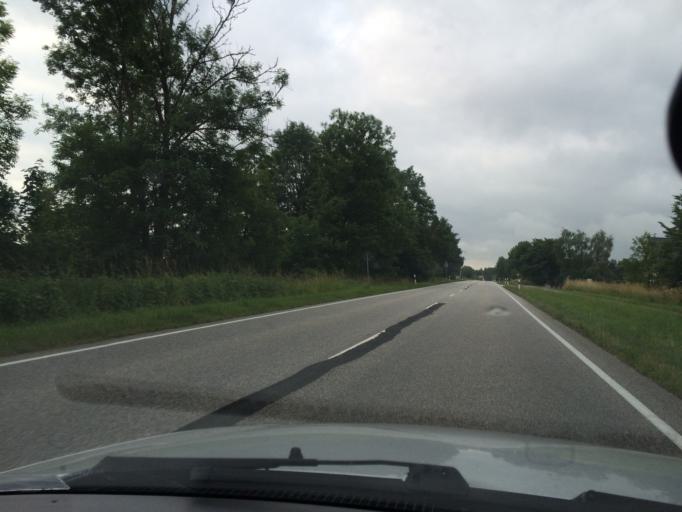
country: DE
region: Schleswig-Holstein
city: Oeversee
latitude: 54.6749
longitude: 9.4389
